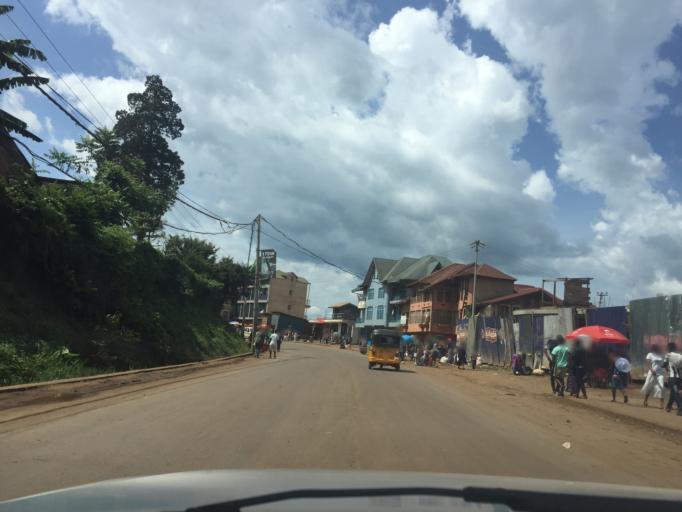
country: CD
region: South Kivu
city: Bukavu
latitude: -2.4958
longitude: 28.8505
